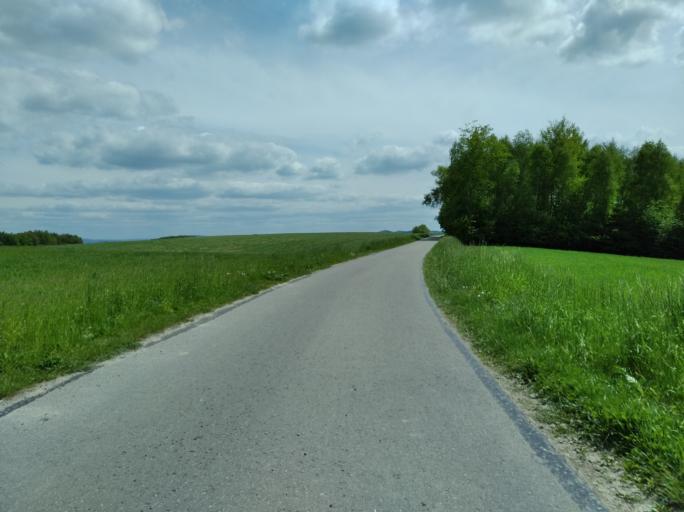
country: PL
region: Subcarpathian Voivodeship
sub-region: Powiat strzyzowski
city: Wisniowa
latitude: 49.8946
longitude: 21.6180
